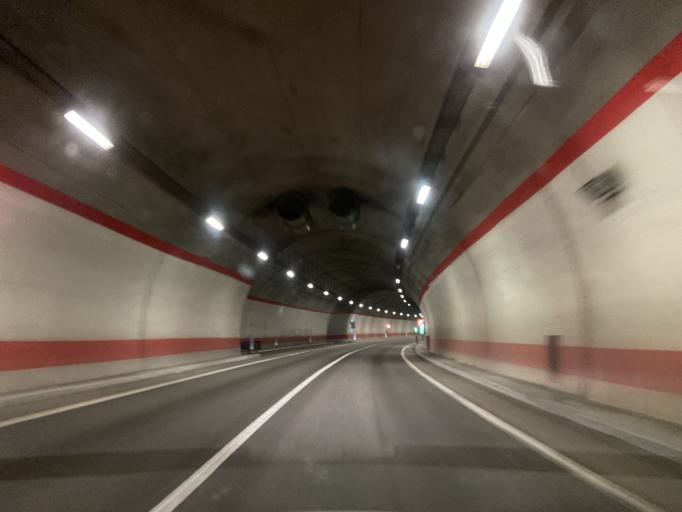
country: IT
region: Piedmont
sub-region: Provincia di Torino
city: Claviere
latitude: 44.9446
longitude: 6.7602
